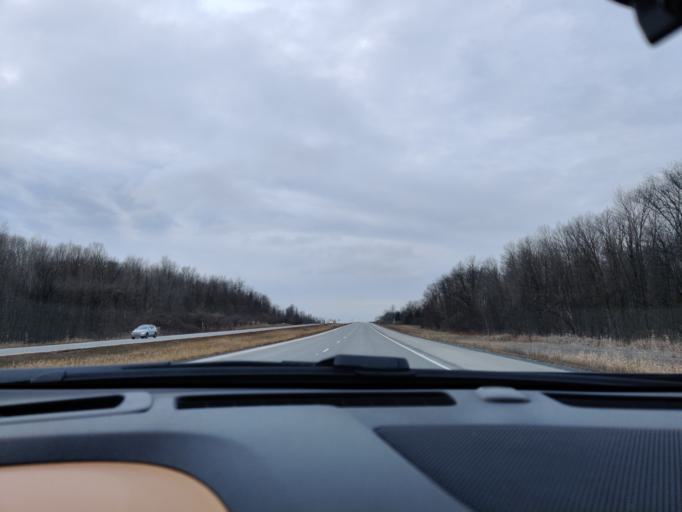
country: CA
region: Ontario
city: Cornwall
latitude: 45.1011
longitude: -74.5718
